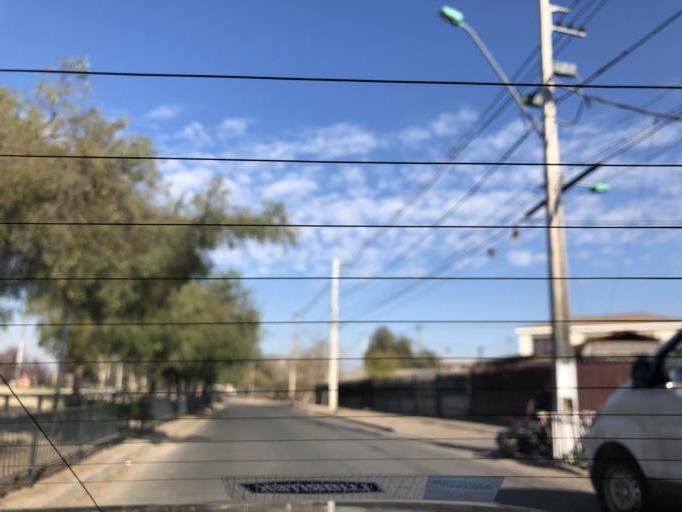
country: CL
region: Santiago Metropolitan
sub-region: Provincia de Cordillera
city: Puente Alto
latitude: -33.6186
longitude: -70.5966
